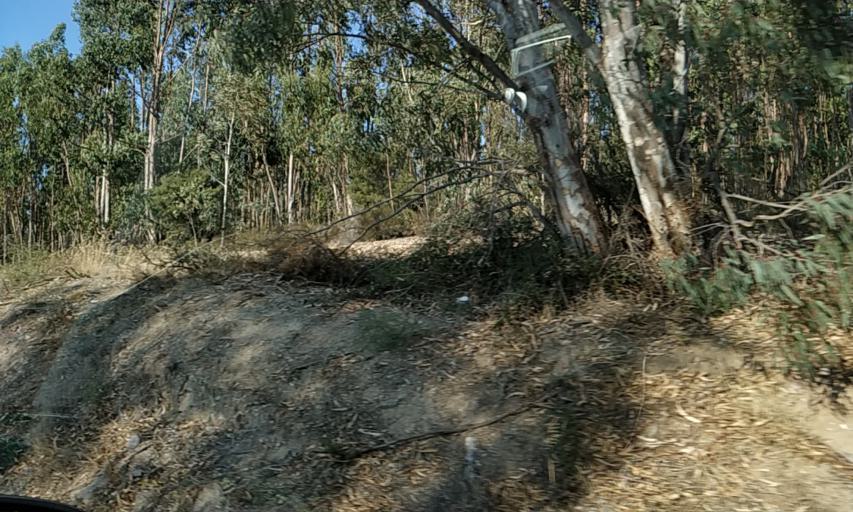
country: PT
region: Santarem
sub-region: Almeirim
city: Fazendas de Almeirim
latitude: 39.1421
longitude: -8.6134
